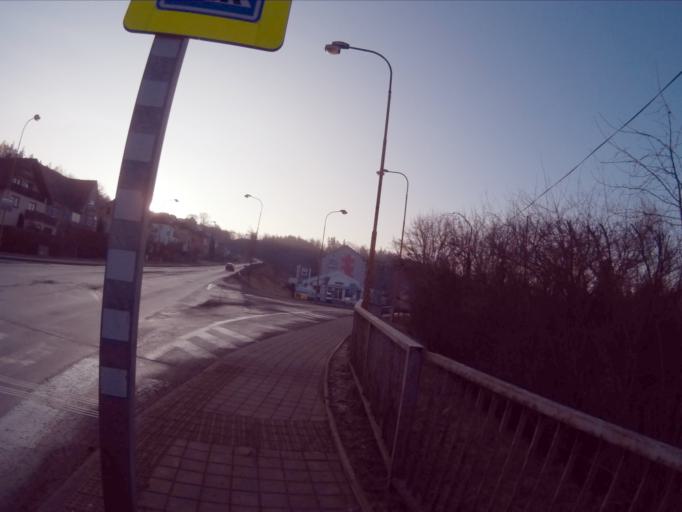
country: CZ
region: Vysocina
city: Namest' nad Oslavou
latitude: 49.2040
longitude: 16.1577
